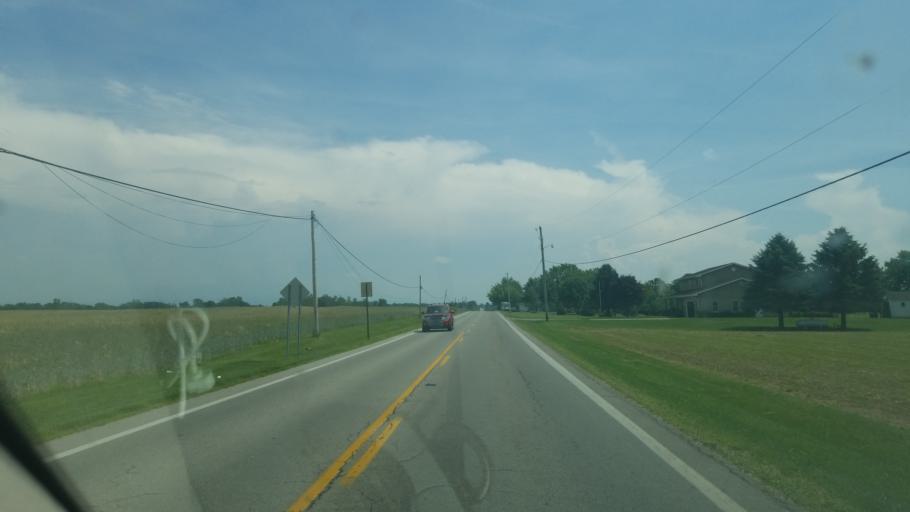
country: US
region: Ohio
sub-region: Logan County
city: Northwood
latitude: 40.5025
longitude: -83.7434
